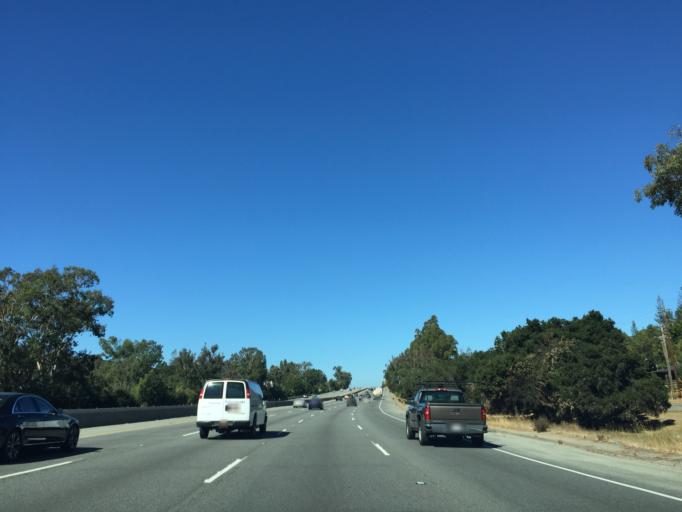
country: US
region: California
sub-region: San Mateo County
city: Emerald Lake Hills
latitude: 37.4454
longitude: -122.2713
